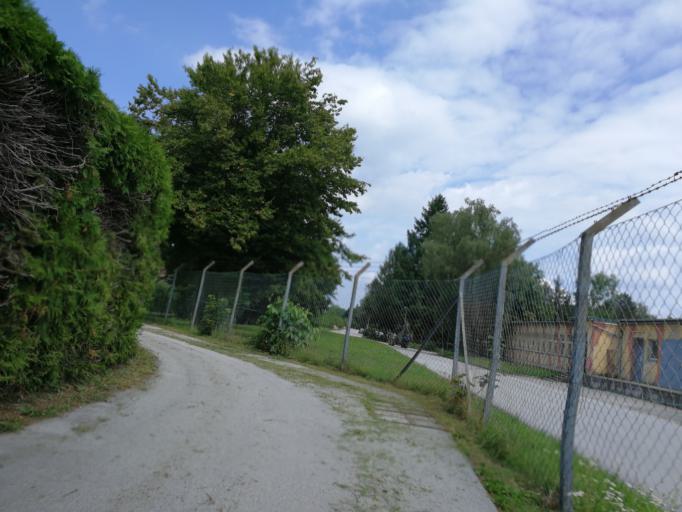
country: DE
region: Bavaria
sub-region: Upper Bavaria
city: Ainring
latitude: 47.8024
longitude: 12.9803
